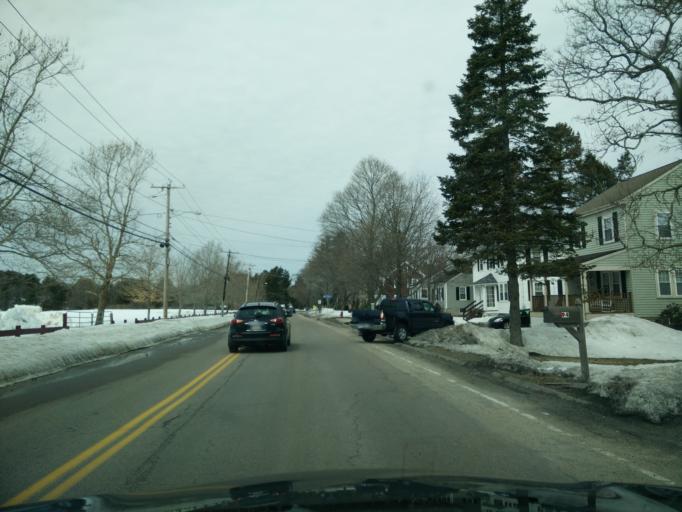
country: US
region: Massachusetts
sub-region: Norfolk County
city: Walpole
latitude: 42.1658
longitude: -71.2372
